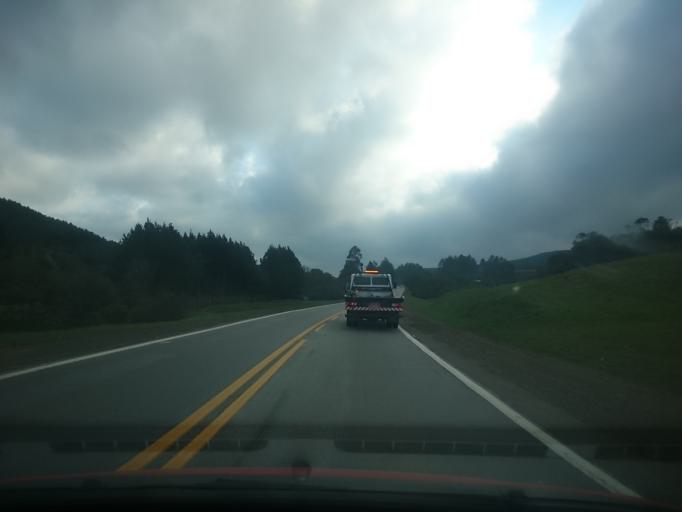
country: BR
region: Santa Catarina
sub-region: Lages
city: Lages
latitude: -27.9227
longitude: -50.4528
